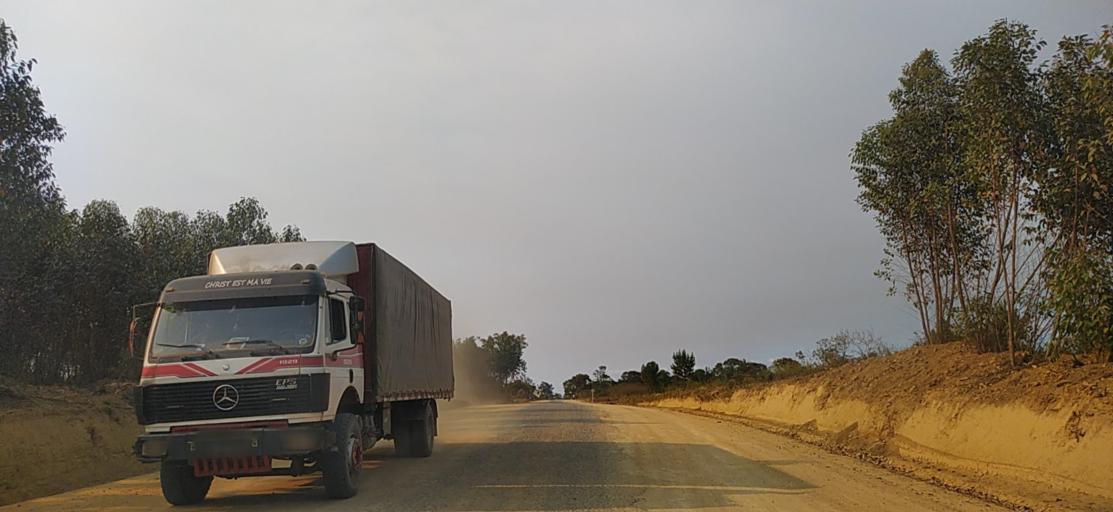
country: MG
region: Alaotra Mangoro
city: Moramanga
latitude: -18.6395
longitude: 48.2757
